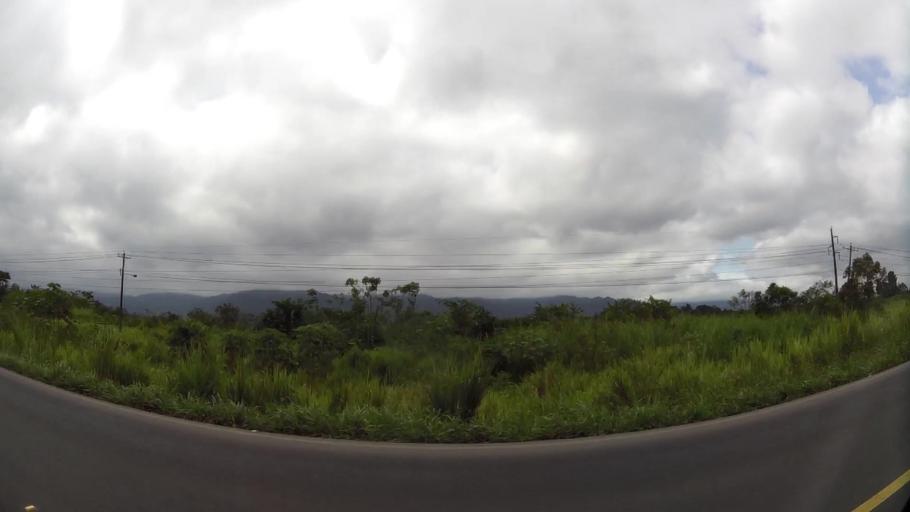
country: EC
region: Guayas
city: Naranjal
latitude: -2.6885
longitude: -79.6383
